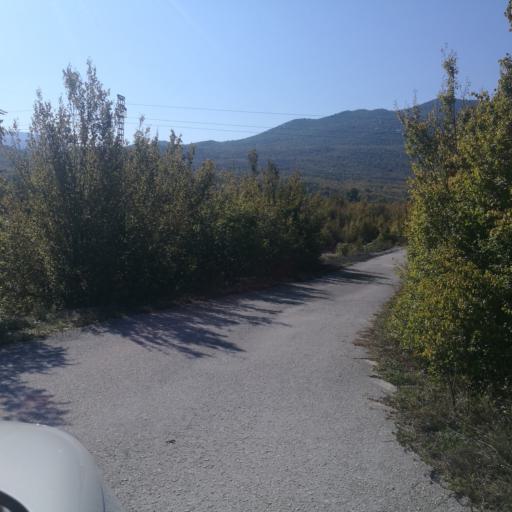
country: HR
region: Splitsko-Dalmatinska
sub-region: Grad Omis
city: Omis
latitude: 43.5180
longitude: 16.7580
